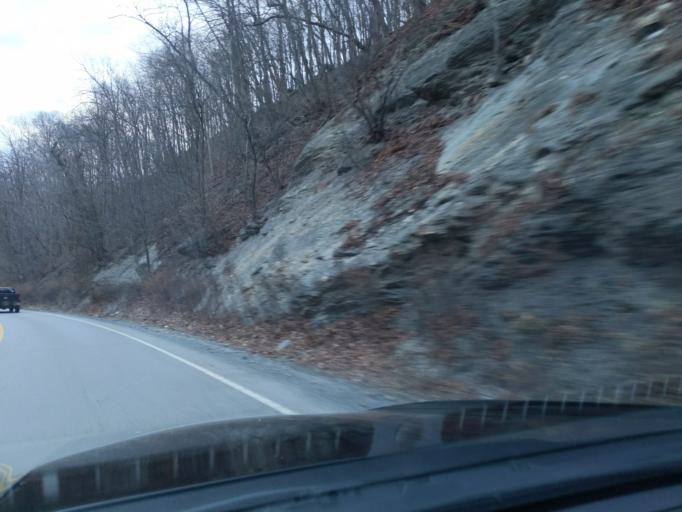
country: US
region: Pennsylvania
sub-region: Blair County
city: Williamsburg
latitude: 40.4844
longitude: -78.2536
